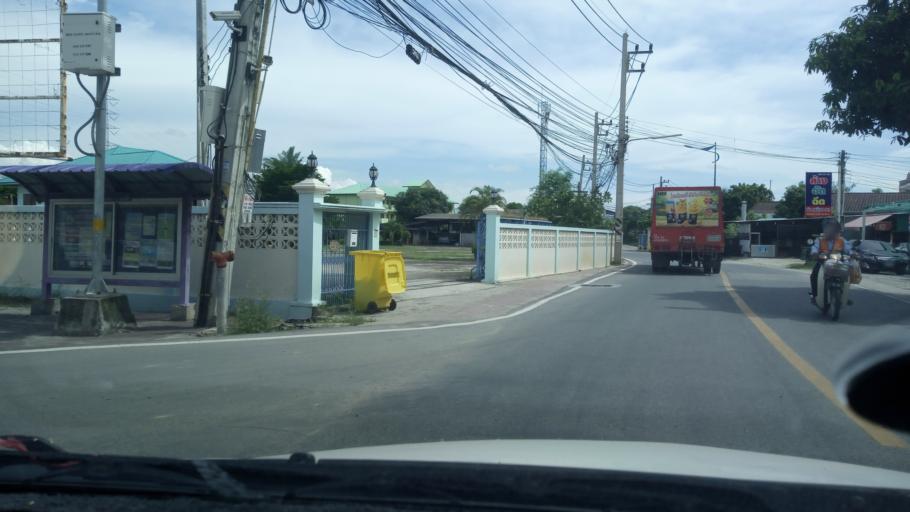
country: TH
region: Chon Buri
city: Phan Thong
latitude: 13.4211
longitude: 101.0341
